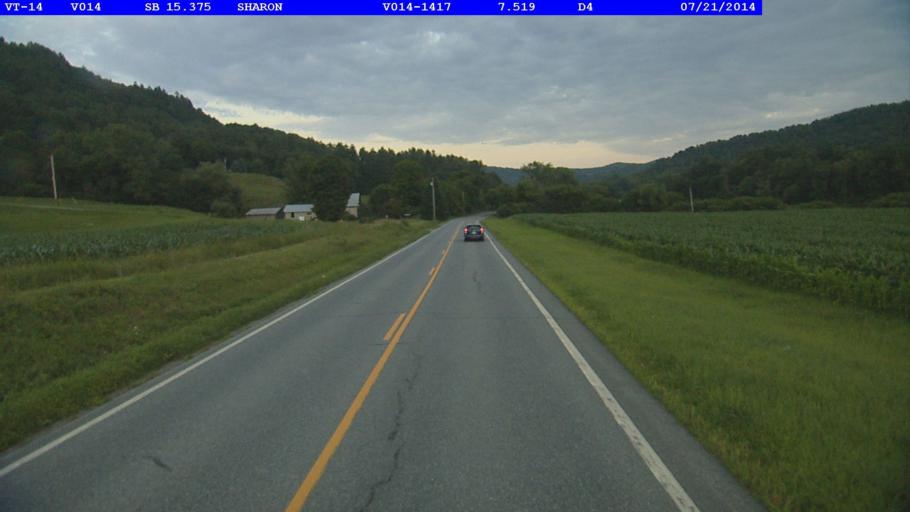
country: US
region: Vermont
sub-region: Windsor County
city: Woodstock
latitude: 43.7953
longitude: -72.4949
